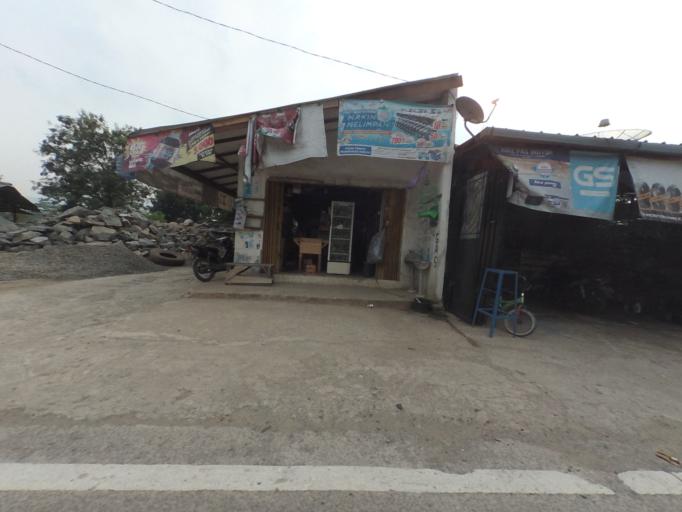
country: ID
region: West Java
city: Sidoger Lebak
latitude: -6.5624
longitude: 106.5799
